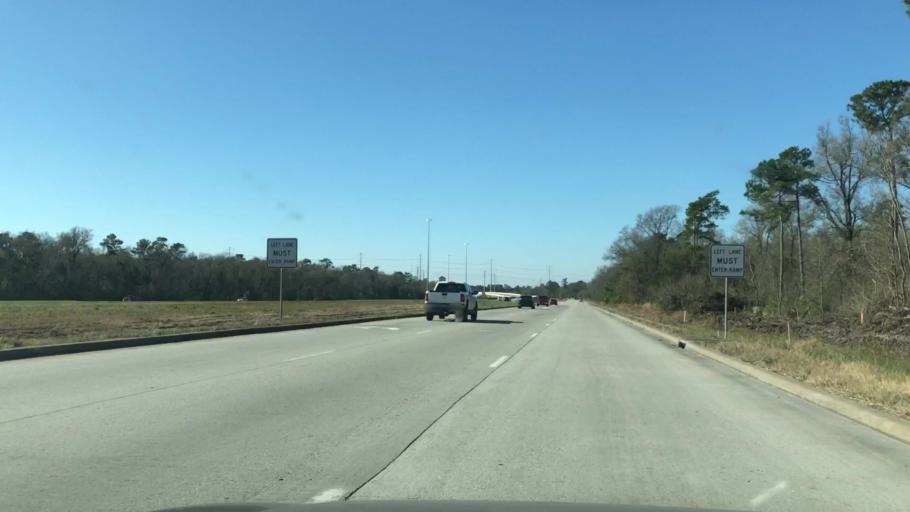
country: US
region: Texas
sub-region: Harris County
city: Cloverleaf
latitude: 29.8237
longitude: -95.1972
